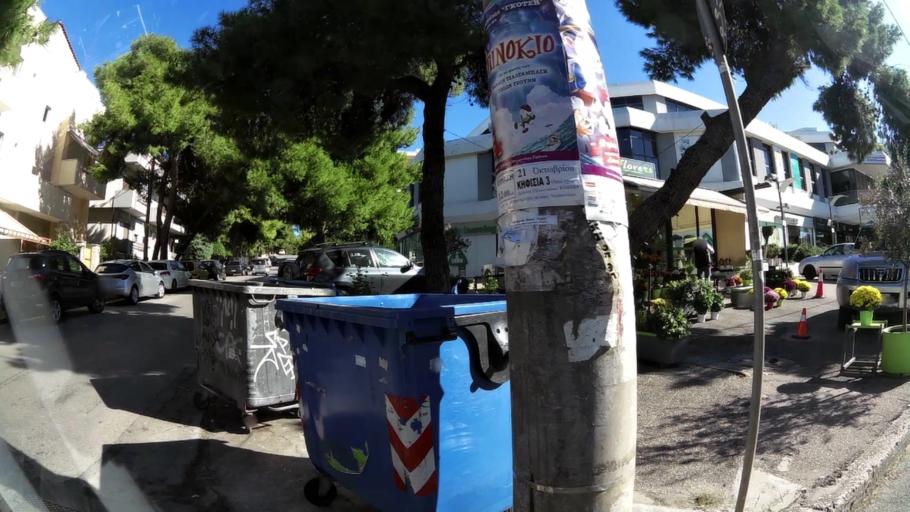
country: GR
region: Attica
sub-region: Nomarchia Athinas
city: Nea Erythraia
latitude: 38.0935
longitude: 23.8093
